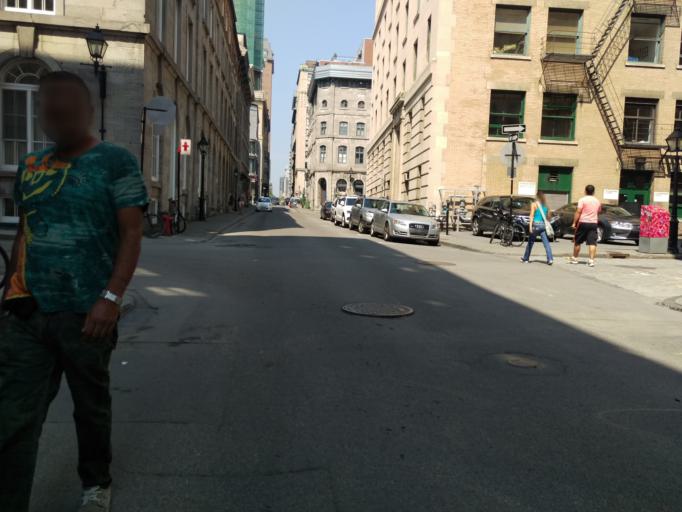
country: CA
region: Quebec
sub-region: Montreal
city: Montreal
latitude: 45.5015
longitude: -73.5568
